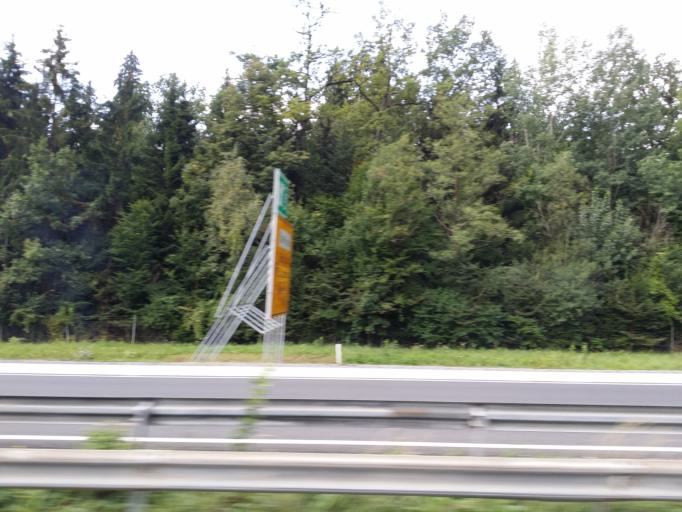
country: SI
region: Kranj
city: Britof
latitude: 46.2456
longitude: 14.3940
